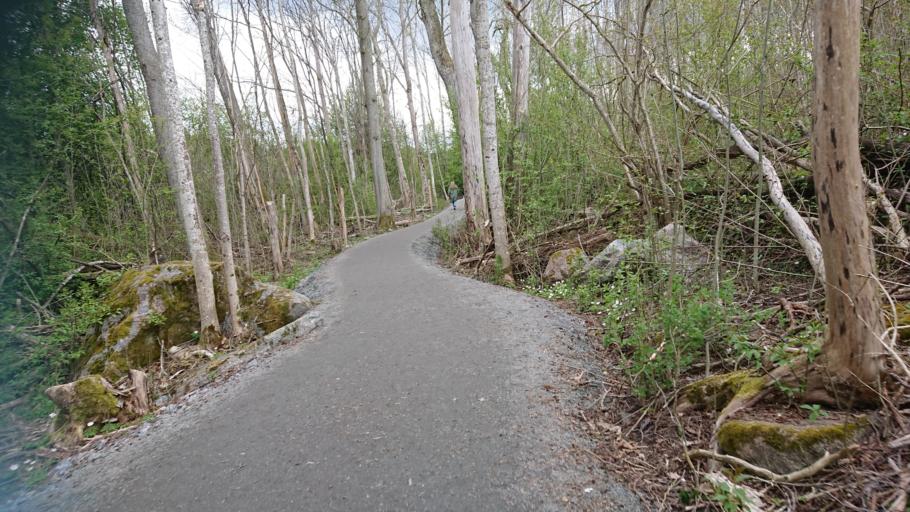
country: SE
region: Uppsala
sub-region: Uppsala Kommun
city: Uppsala
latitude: 59.7965
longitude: 17.6106
